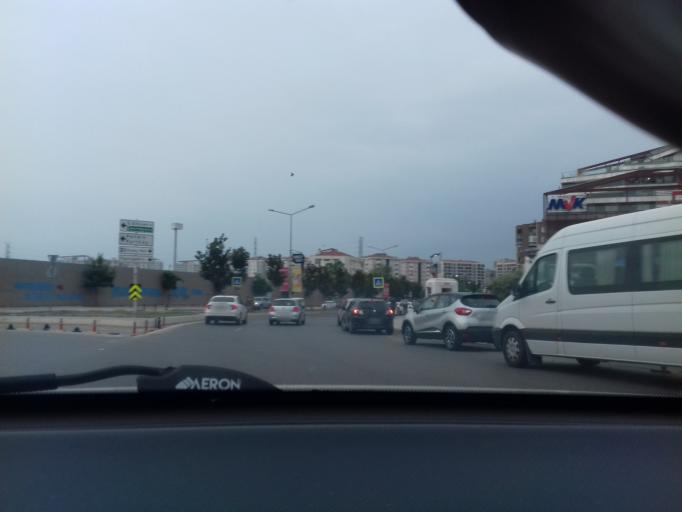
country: TR
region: Istanbul
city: Sultanbeyli
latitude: 40.9275
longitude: 29.3098
